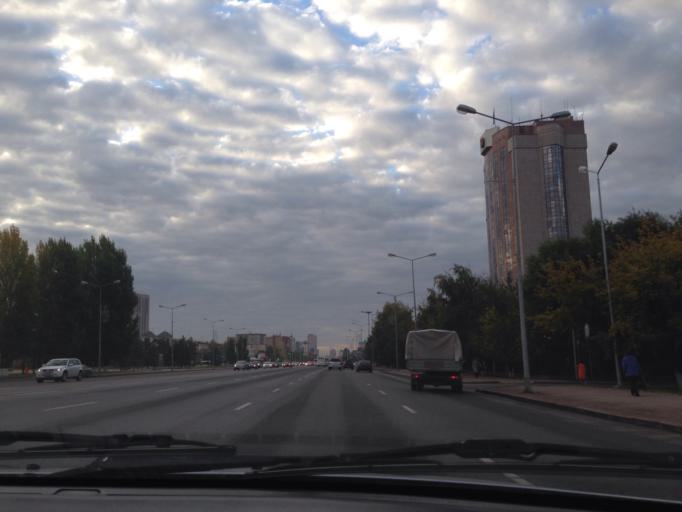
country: KZ
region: Astana Qalasy
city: Astana
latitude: 51.1539
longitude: 71.4542
